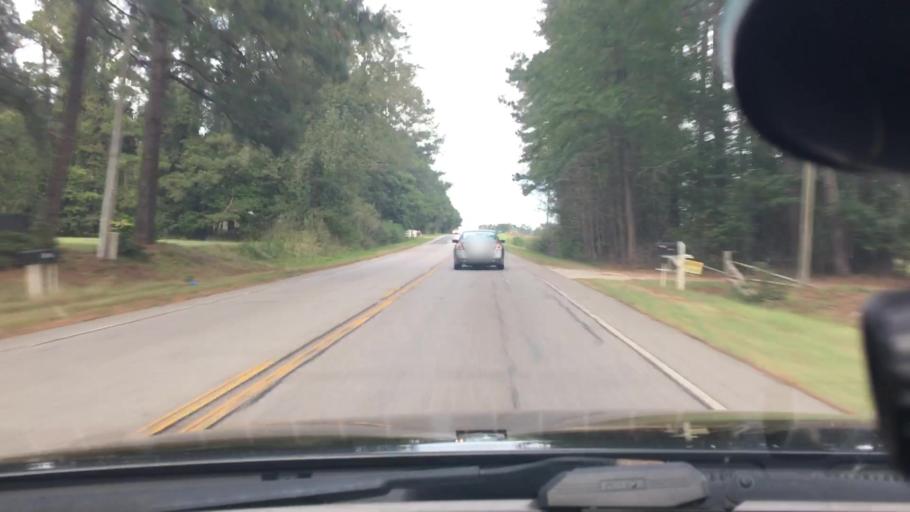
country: US
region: North Carolina
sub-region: Moore County
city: Carthage
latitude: 35.3582
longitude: -79.3334
